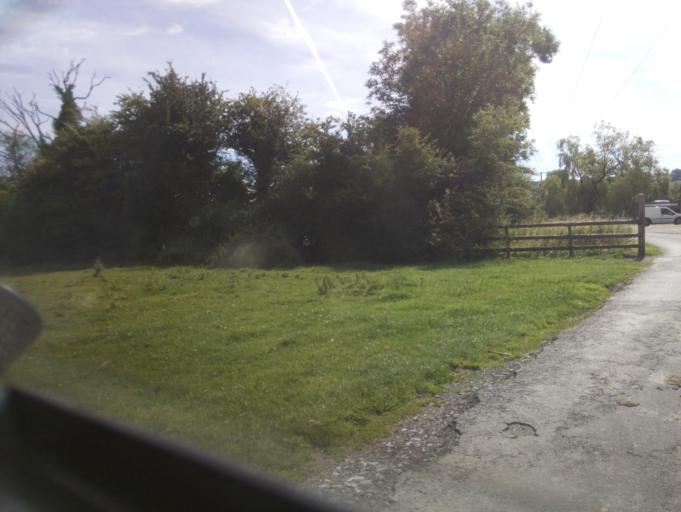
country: GB
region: England
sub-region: South Gloucestershire
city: Chipping Sodbury
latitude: 51.5430
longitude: -2.3712
